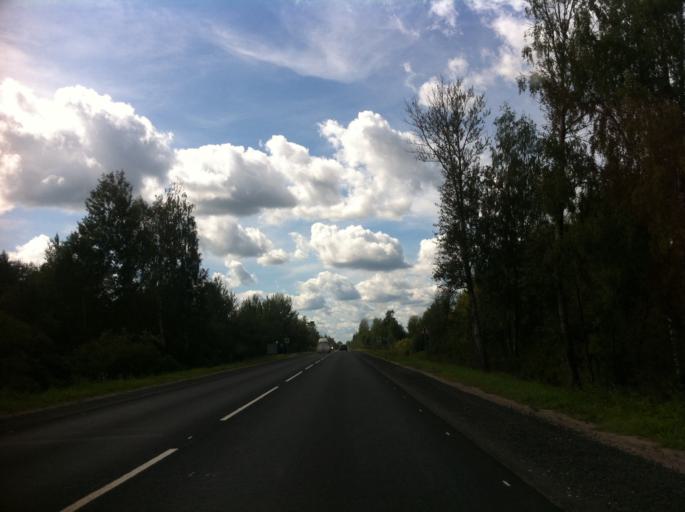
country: RU
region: Pskov
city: Izborsk
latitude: 57.7473
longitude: 28.0371
